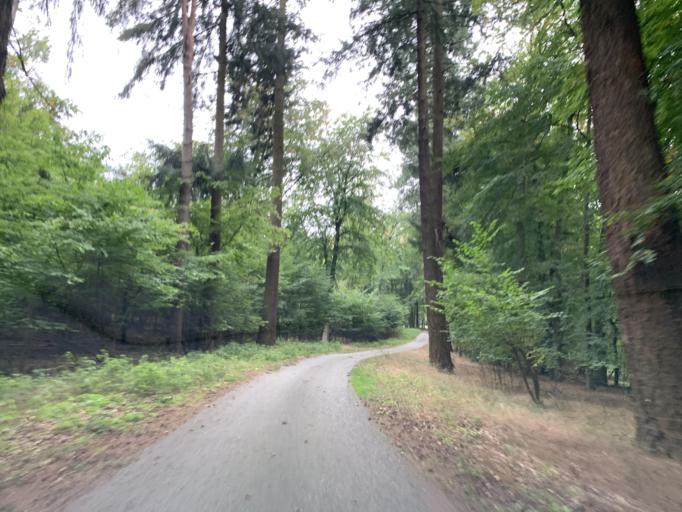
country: DE
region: Mecklenburg-Vorpommern
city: Woldegk
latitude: 53.3218
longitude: 13.6088
